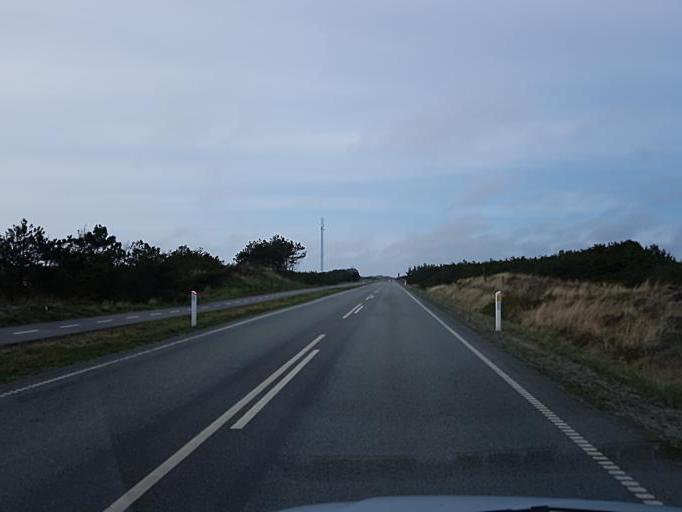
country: DK
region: Central Jutland
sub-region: Ringkobing-Skjern Kommune
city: Hvide Sande
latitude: 55.9467
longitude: 8.1544
